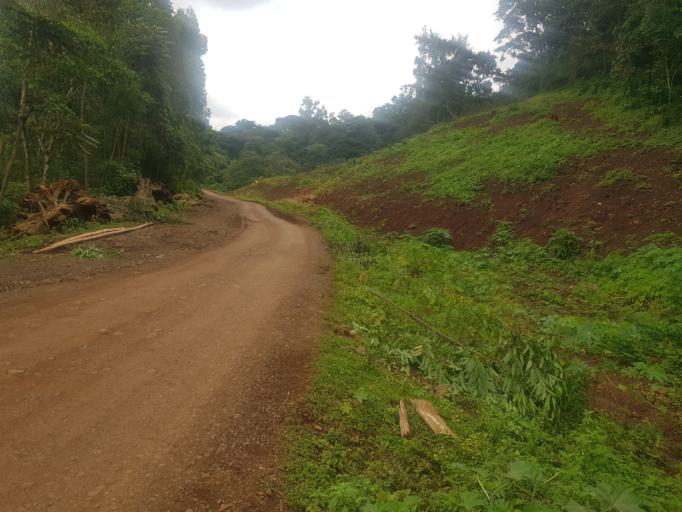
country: ET
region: Oromiya
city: Gore
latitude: 7.8275
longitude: 35.4633
